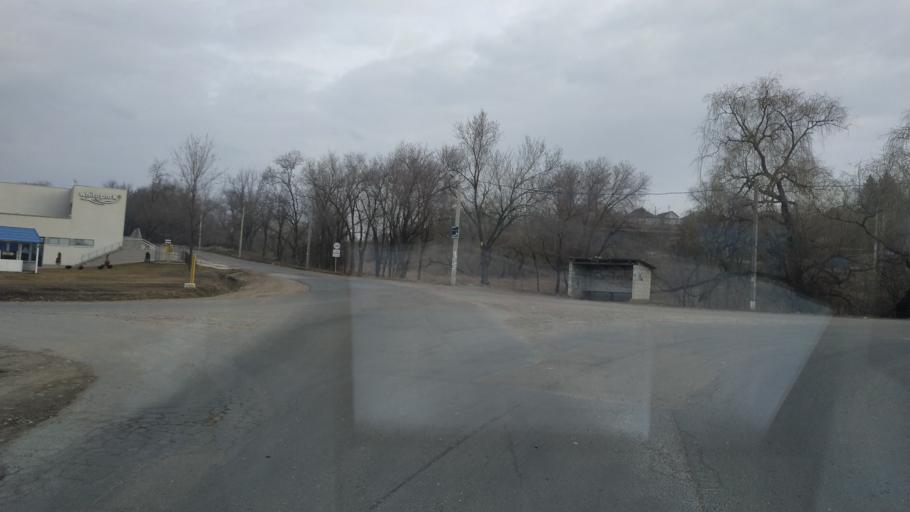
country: MD
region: Chisinau
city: Singera
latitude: 46.9265
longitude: 29.0489
